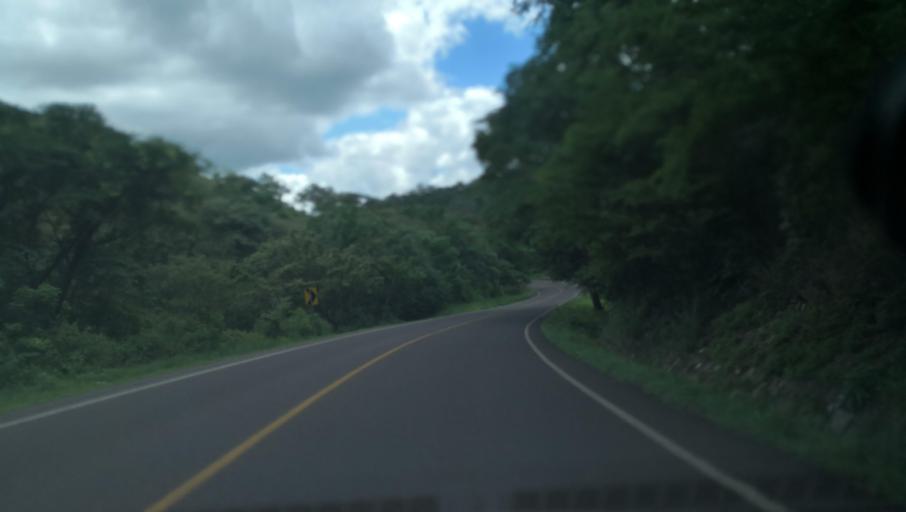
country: NI
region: Madriz
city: Palacaguina
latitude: 13.4376
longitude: -86.4349
